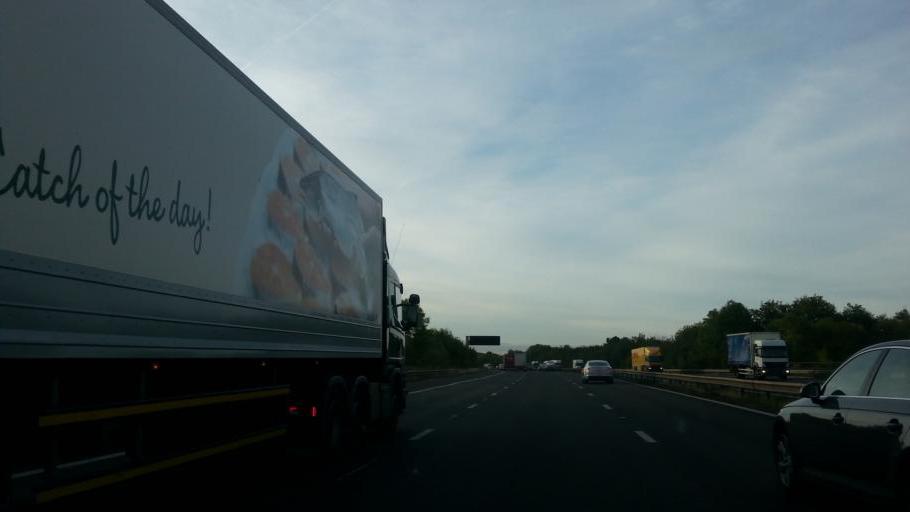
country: GB
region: England
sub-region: Leicestershire
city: Cosby
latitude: 52.5484
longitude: -1.1858
